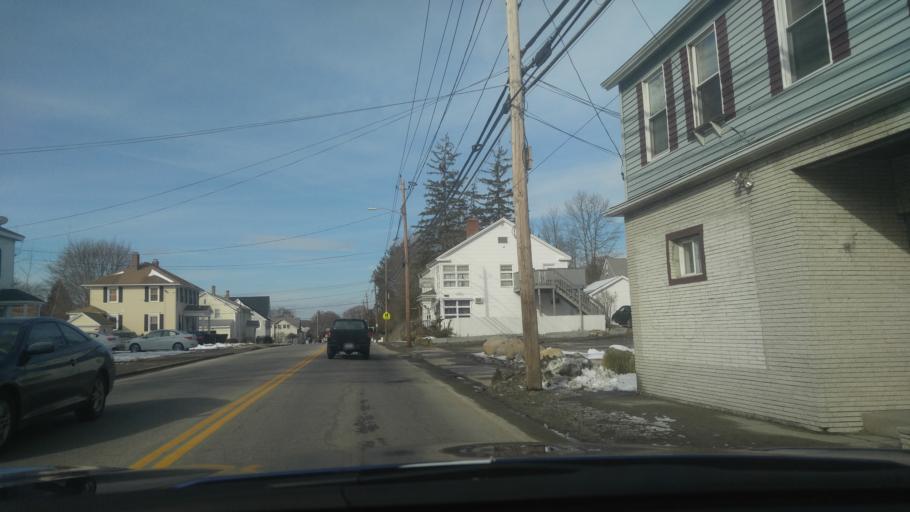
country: US
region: Rhode Island
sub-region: Kent County
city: West Warwick
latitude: 41.6881
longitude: -71.5223
